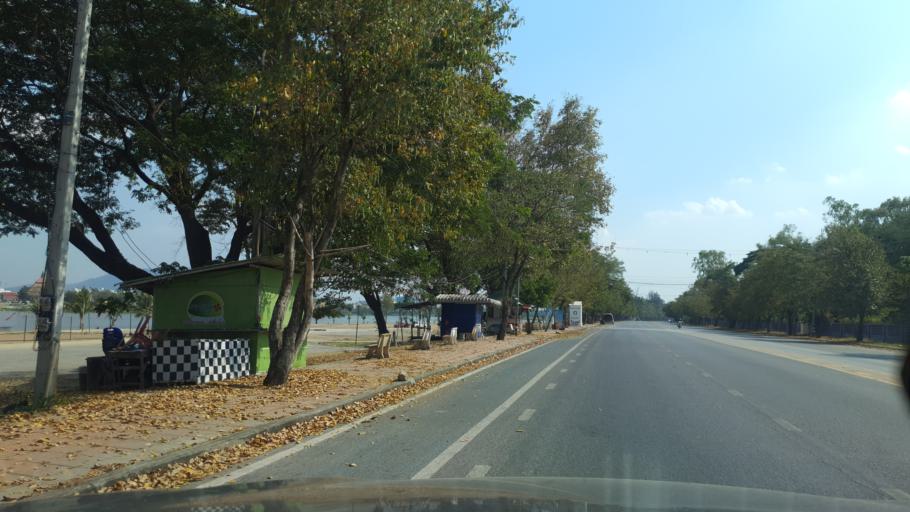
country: TH
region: Tak
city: Tak
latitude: 16.8806
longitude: 99.1146
